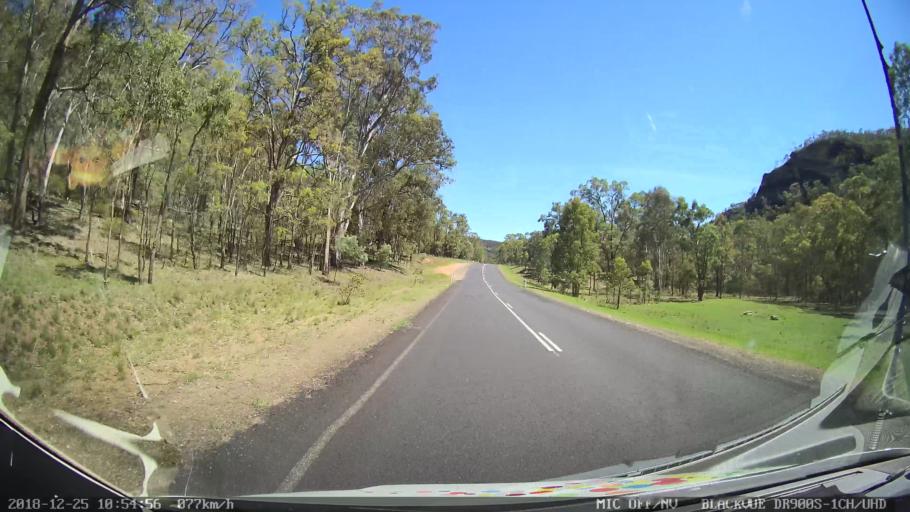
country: AU
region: New South Wales
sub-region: Upper Hunter Shire
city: Merriwa
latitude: -32.4044
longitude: 150.2733
